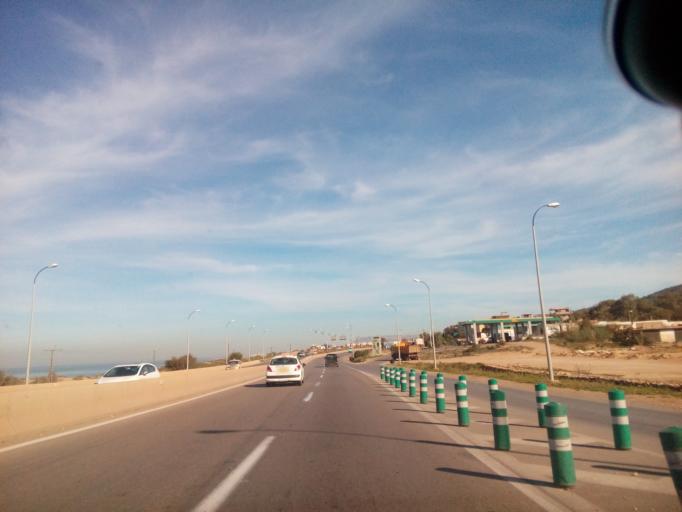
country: DZ
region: Mostaganem
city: Mostaganem
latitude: 35.8721
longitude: 0.0401
